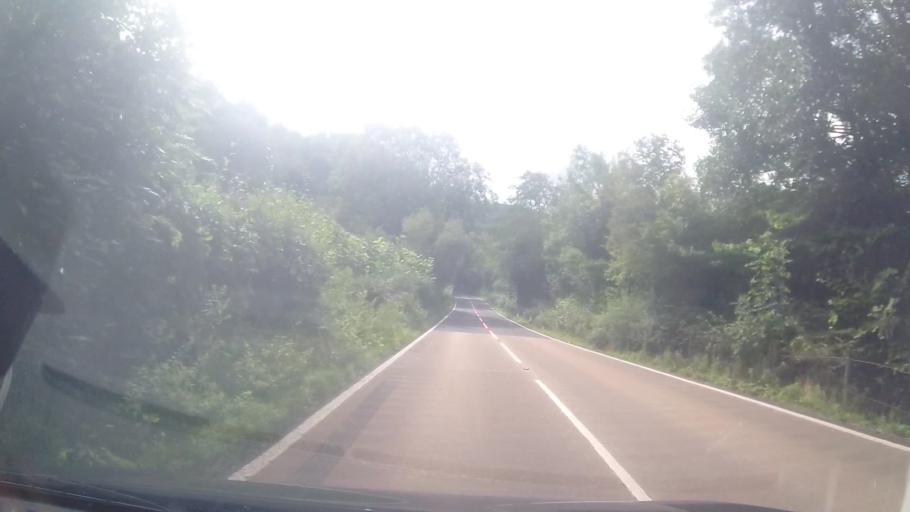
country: GB
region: Wales
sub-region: Sir Powys
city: Machynlleth
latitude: 52.5654
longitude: -3.9141
